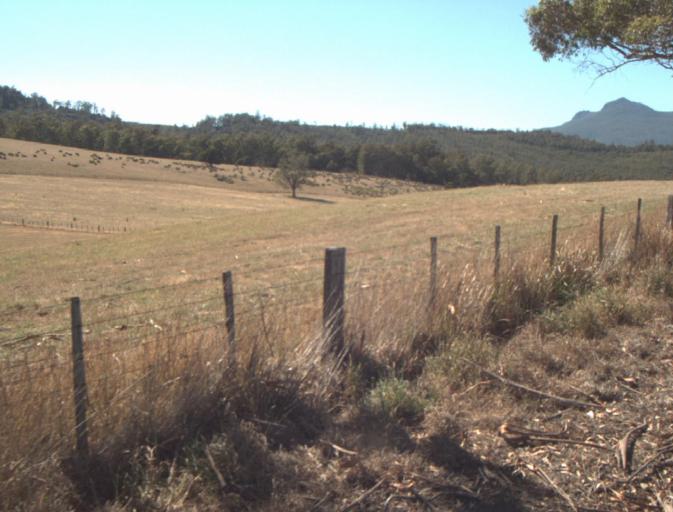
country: AU
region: Tasmania
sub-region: Launceston
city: Newstead
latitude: -41.3109
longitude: 147.3208
